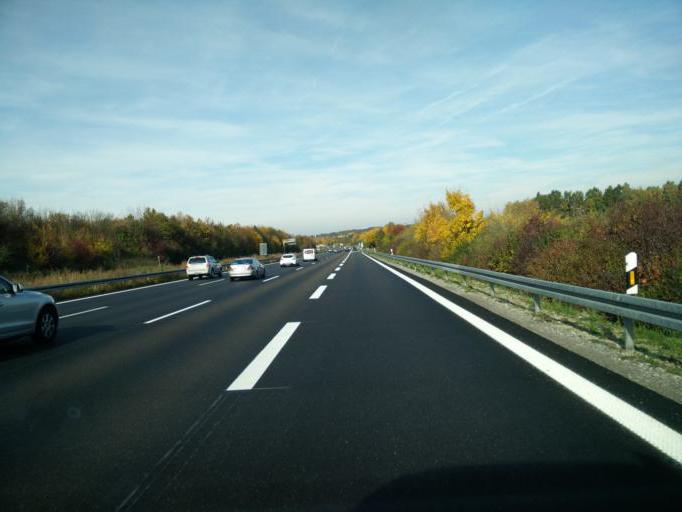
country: DE
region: Baden-Wuerttemberg
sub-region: Karlsruhe Region
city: Ettlingen
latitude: 48.9533
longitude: 8.4847
